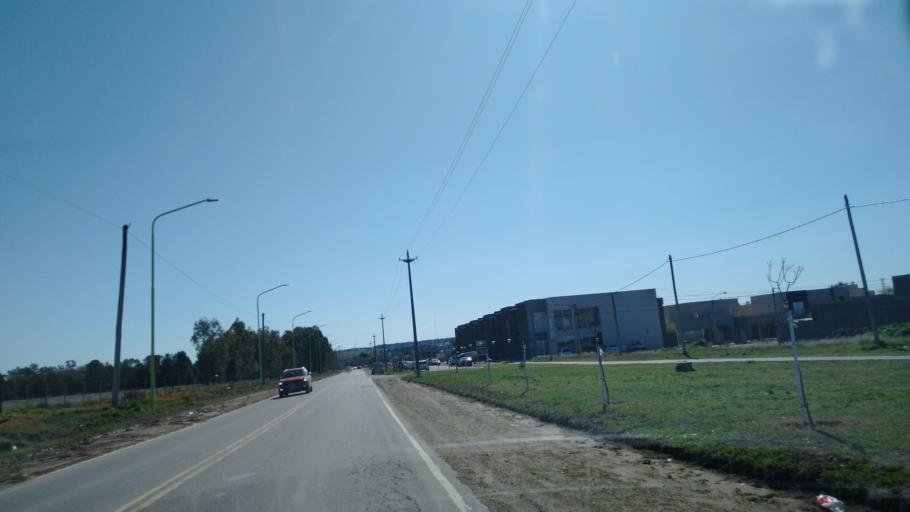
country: AR
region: Buenos Aires
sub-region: Partido de Bahia Blanca
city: Bahia Blanca
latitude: -38.6947
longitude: -62.2303
